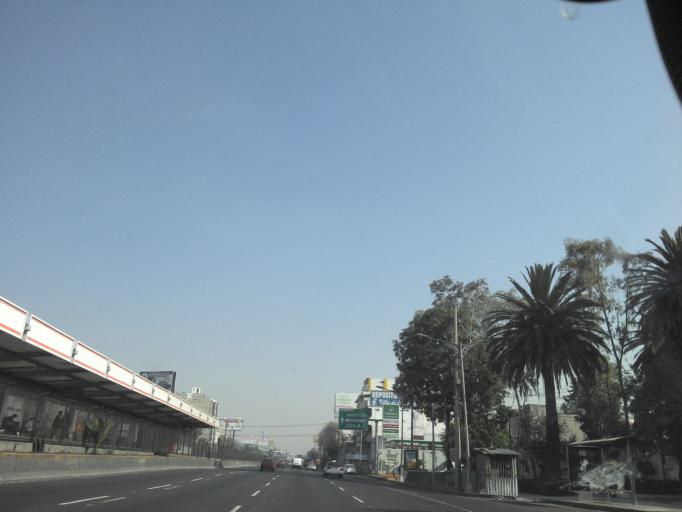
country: MX
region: Mexico City
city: Colonia Nativitas
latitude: 19.3876
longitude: -99.1388
